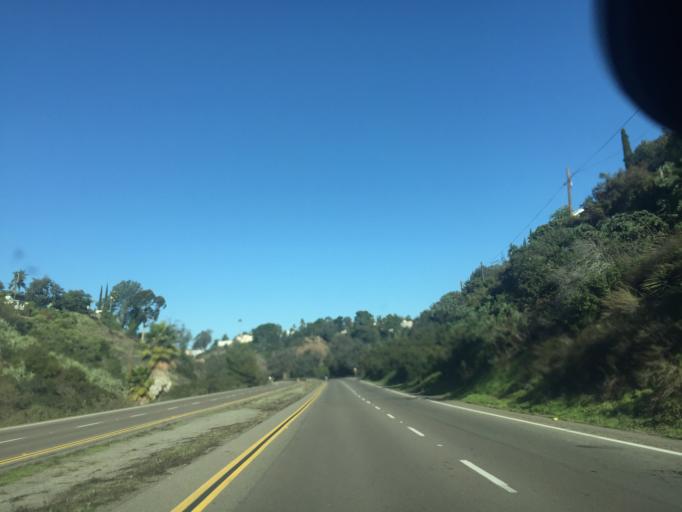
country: US
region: California
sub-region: San Diego County
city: Lemon Grove
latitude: 32.7607
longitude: -117.0993
